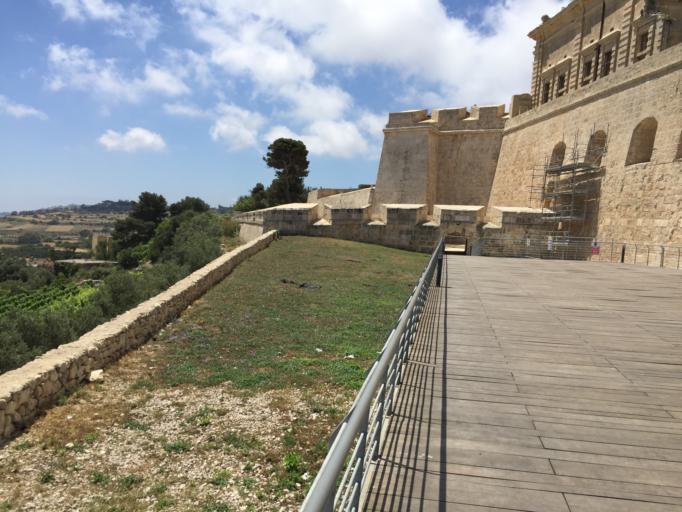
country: MT
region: L-Imdina
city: Imdina
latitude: 35.8851
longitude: 14.4046
